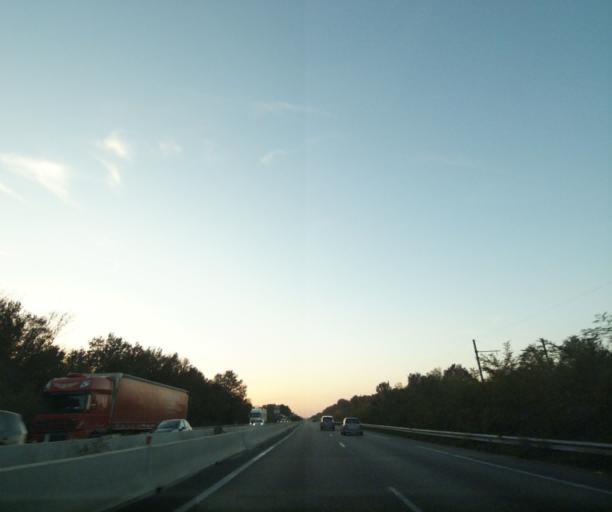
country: FR
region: Provence-Alpes-Cote d'Azur
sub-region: Departement des Bouches-du-Rhone
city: Saint-Martin-de-Crau
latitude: 43.6380
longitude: 4.7306
